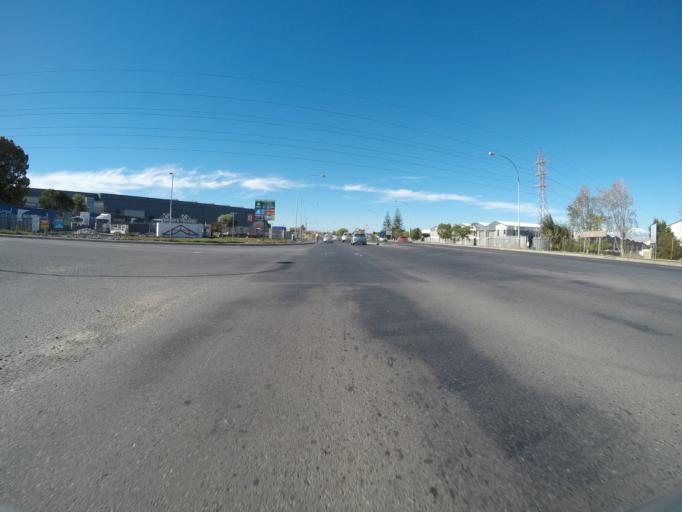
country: ZA
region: Western Cape
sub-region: City of Cape Town
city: Kraaifontein
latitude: -33.8969
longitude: 18.6714
